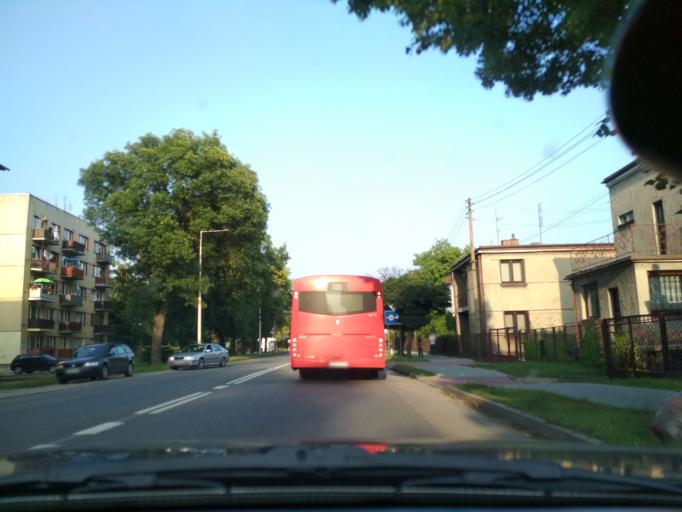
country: PL
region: Silesian Voivodeship
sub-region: Powiat zawiercianski
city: Zawiercie
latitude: 50.4779
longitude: 19.4536
